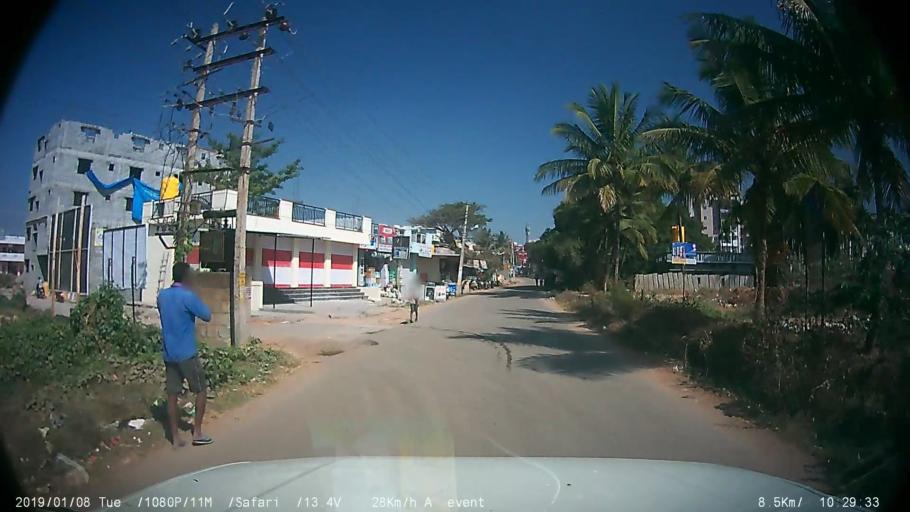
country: IN
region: Karnataka
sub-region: Bangalore Urban
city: Anekal
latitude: 12.8305
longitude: 77.6551
